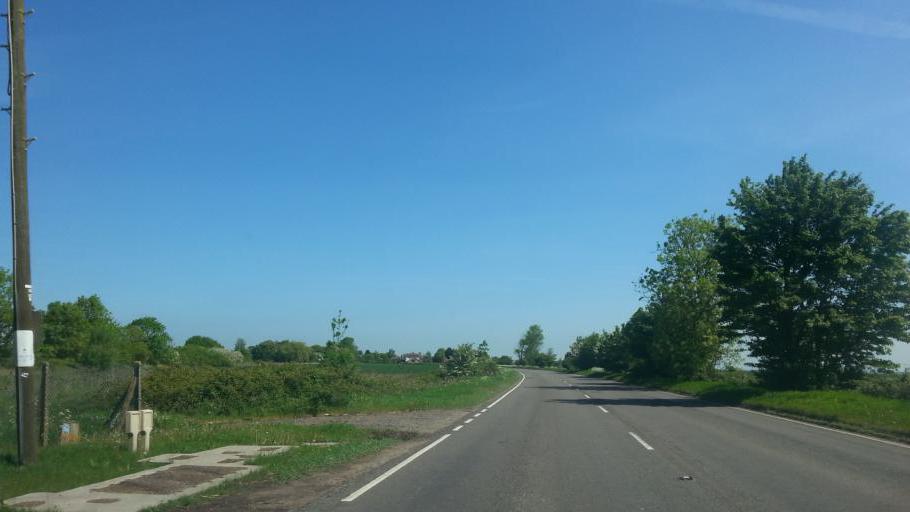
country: GB
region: England
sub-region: Cambridgeshire
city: Warboys
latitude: 52.3962
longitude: -0.0756
